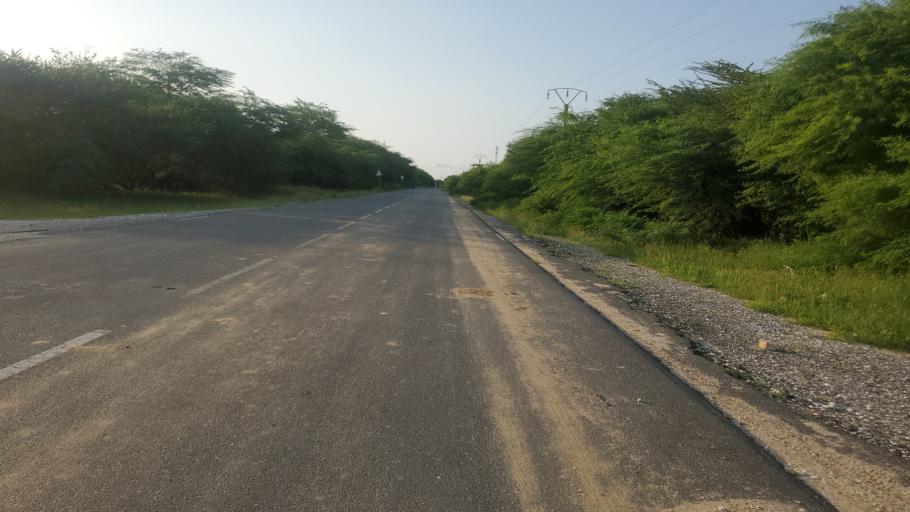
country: SN
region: Saint-Louis
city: Saint-Louis
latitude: 16.2000
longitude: -16.4114
